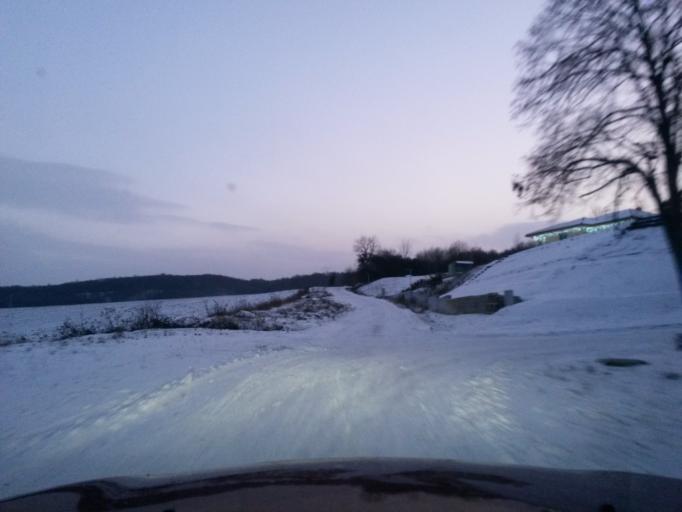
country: SK
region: Kosicky
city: Kosice
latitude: 48.7440
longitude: 21.3187
